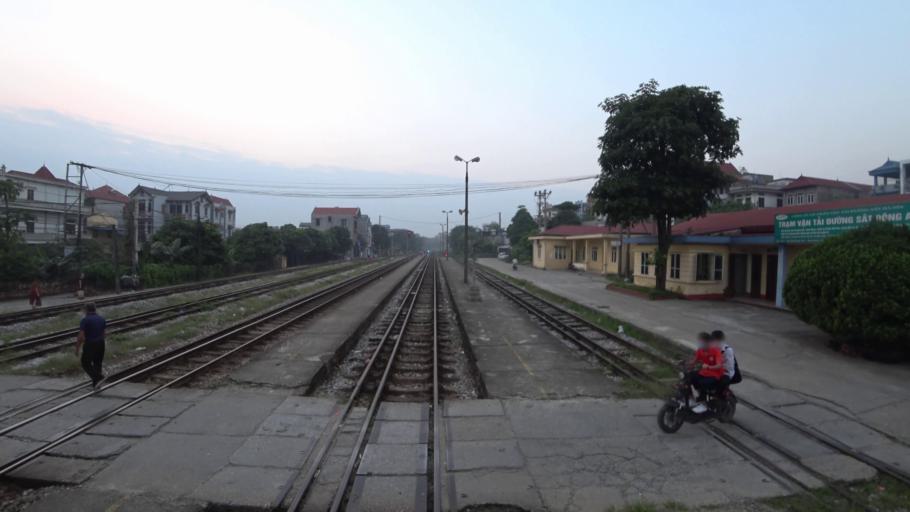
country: VN
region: Ha Noi
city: Dong Anh
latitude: 21.1831
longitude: 105.8539
